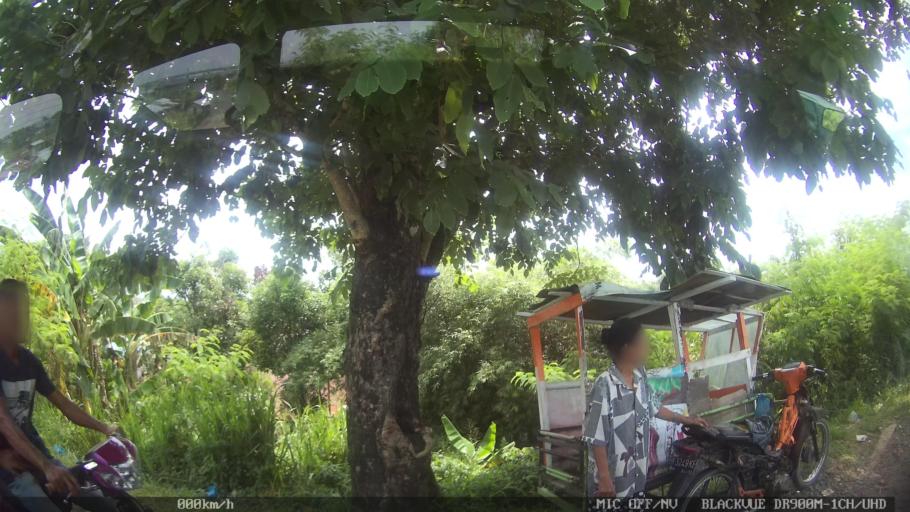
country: ID
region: North Sumatra
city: Medan
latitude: 3.6462
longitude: 98.6876
